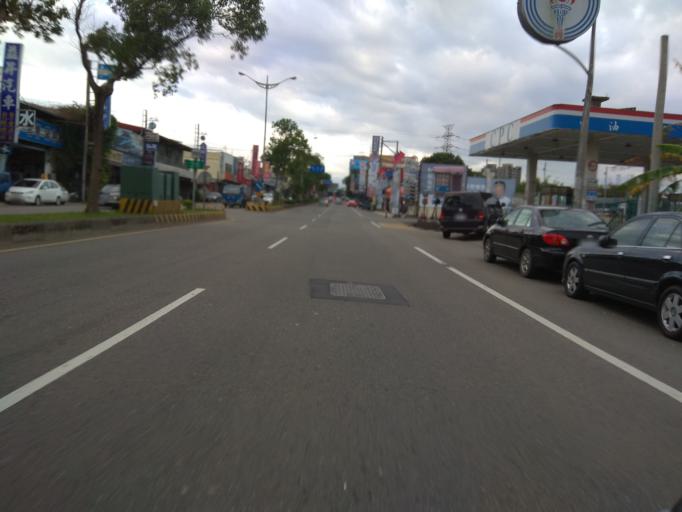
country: TW
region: Taiwan
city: Daxi
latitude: 24.8731
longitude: 121.2137
